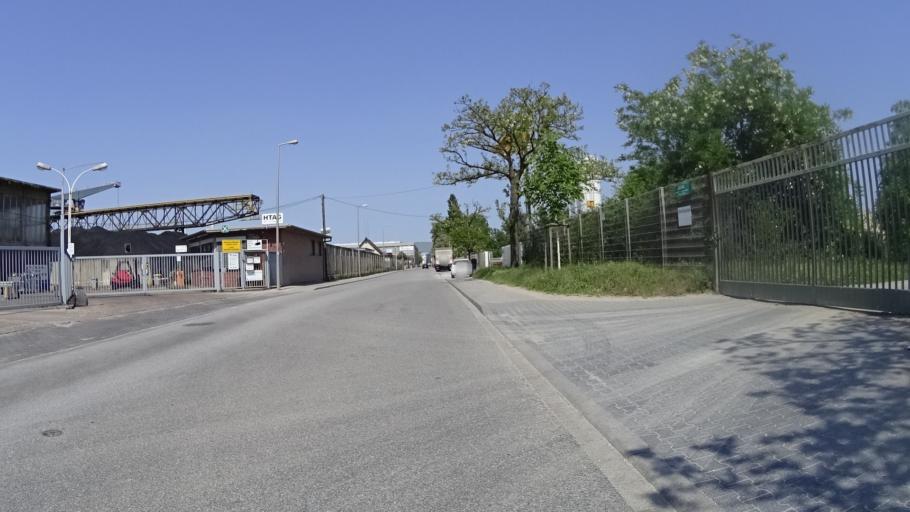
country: DE
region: Rheinland-Pfalz
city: Altrip
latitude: 49.4277
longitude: 8.5183
